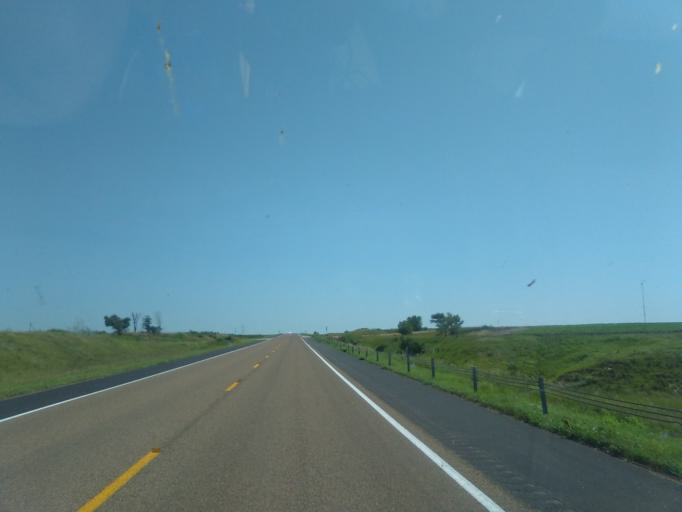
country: US
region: Nebraska
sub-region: Hitchcock County
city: Trenton
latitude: 40.2192
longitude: -100.9394
